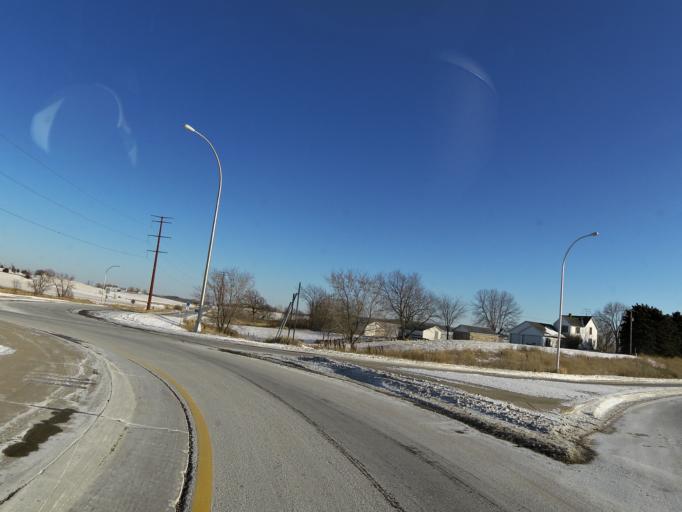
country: US
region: Minnesota
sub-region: Le Sueur County
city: New Prague
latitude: 44.5724
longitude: -93.5054
